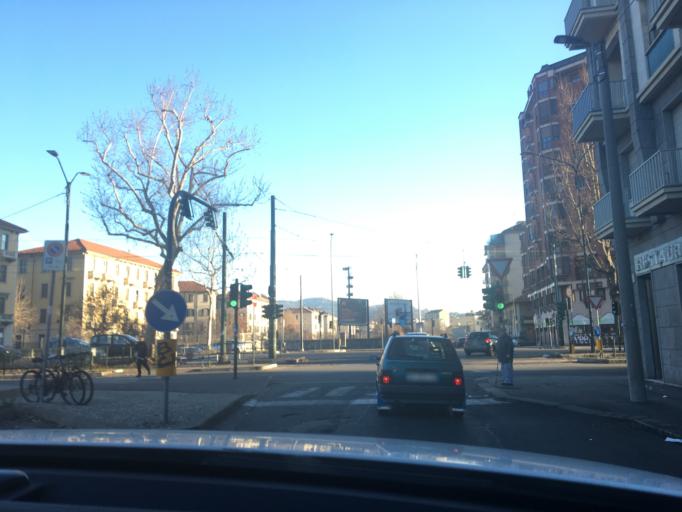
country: IT
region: Piedmont
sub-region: Provincia di Torino
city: Turin
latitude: 45.0487
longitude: 7.6636
